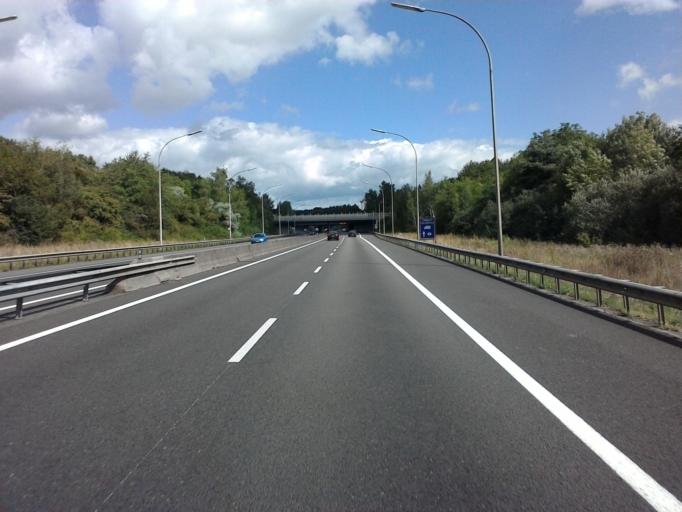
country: LU
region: Luxembourg
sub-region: Canton de Luxembourg
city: Strassen
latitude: 49.6152
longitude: 6.0830
